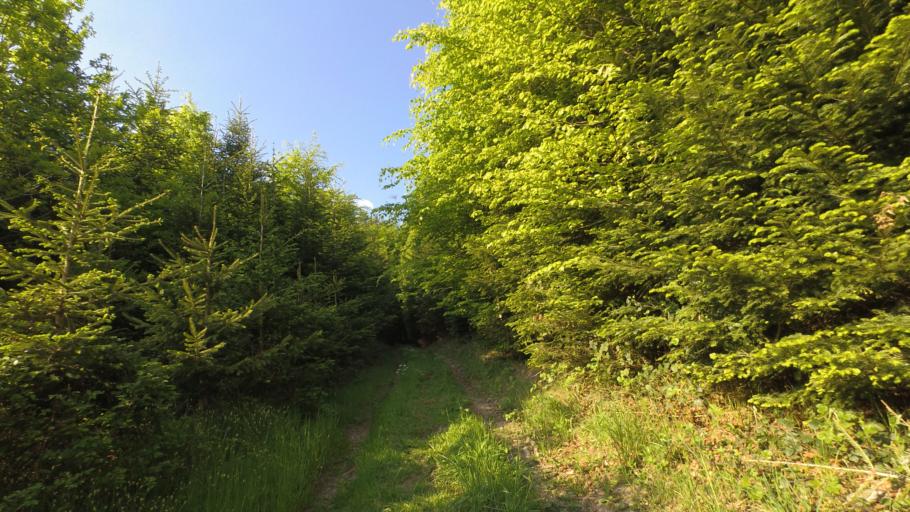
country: DE
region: Bavaria
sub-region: Upper Bavaria
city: Nussdorf
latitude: 47.8935
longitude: 12.5805
